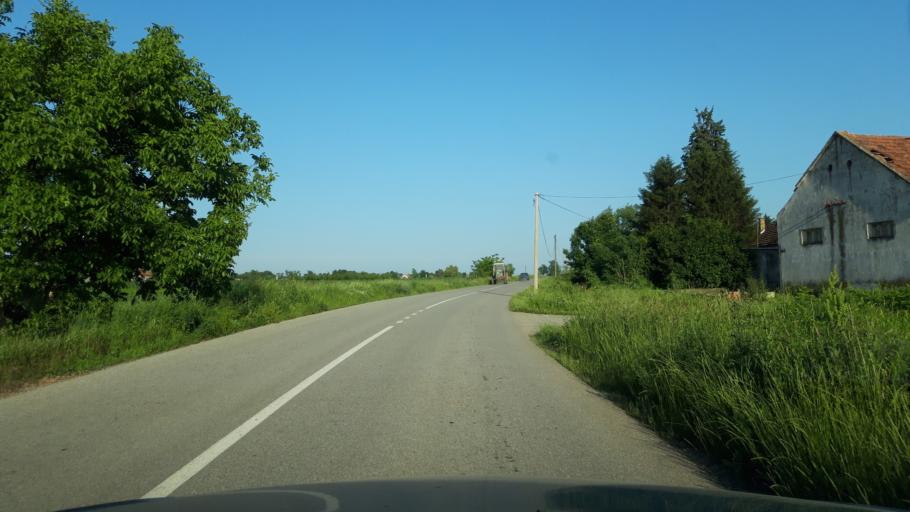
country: RS
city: Celarevo
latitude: 45.1052
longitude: 19.4969
